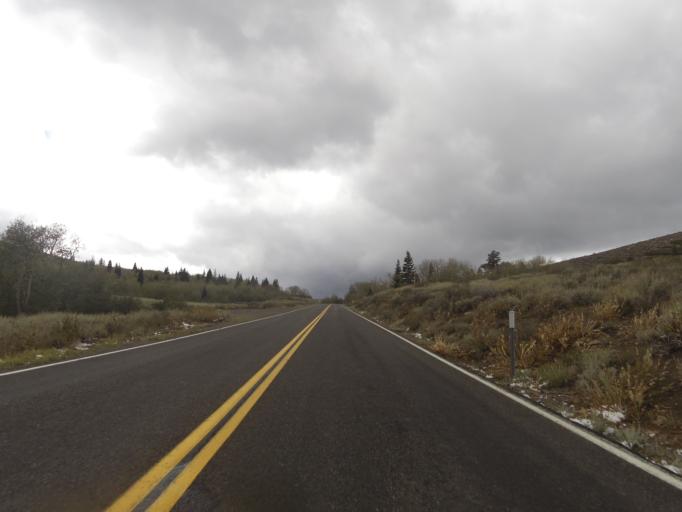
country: US
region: Nevada
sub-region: Douglas County
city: Gardnerville Ranchos
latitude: 38.6738
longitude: -119.6079
